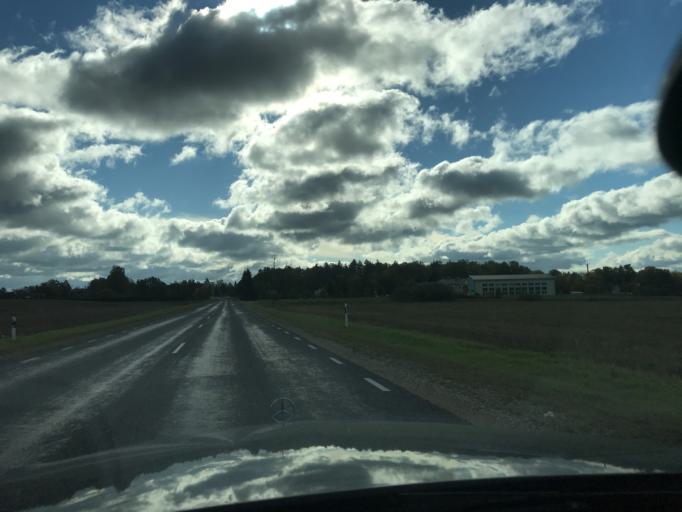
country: EE
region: Vorumaa
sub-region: Antsla vald
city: Vana-Antsla
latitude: 57.9604
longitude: 26.2725
